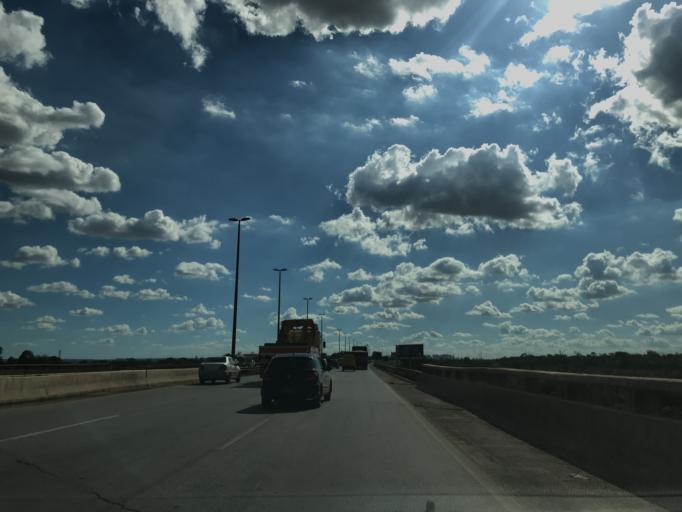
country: BR
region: Federal District
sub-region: Brasilia
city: Brasilia
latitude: -15.7896
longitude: -47.9502
